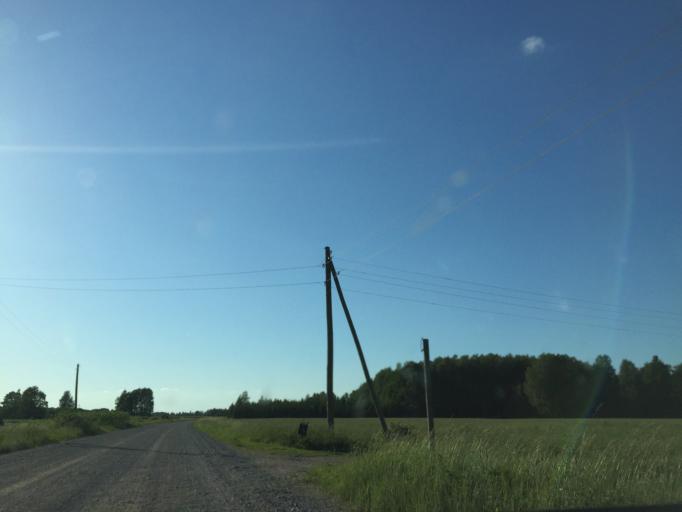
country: LV
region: Kandava
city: Kandava
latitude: 56.8378
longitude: 22.7172
